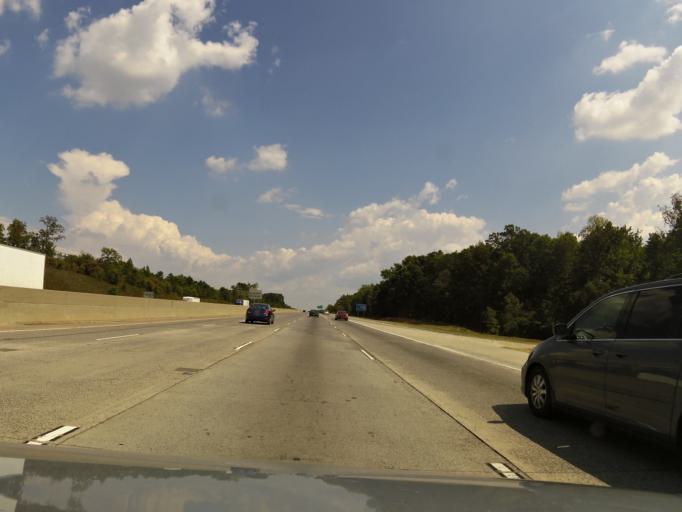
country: US
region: North Carolina
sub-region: Gaston County
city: Mount Holly
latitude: 35.2475
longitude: -80.9651
